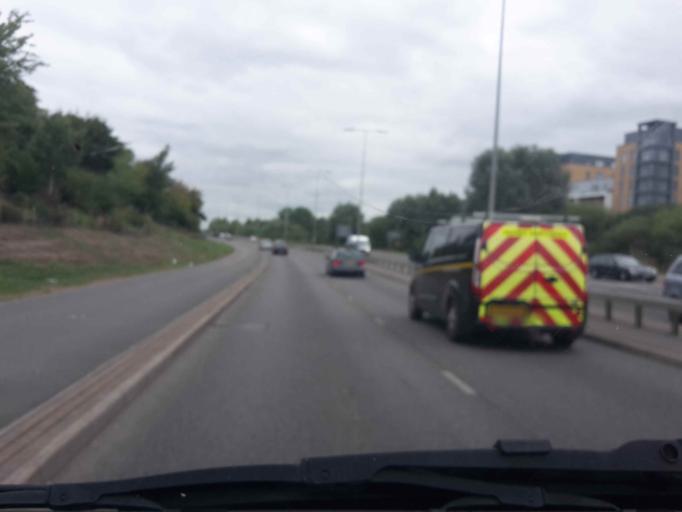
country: GB
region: England
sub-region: Reading
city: Reading
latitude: 51.4317
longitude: -0.9785
